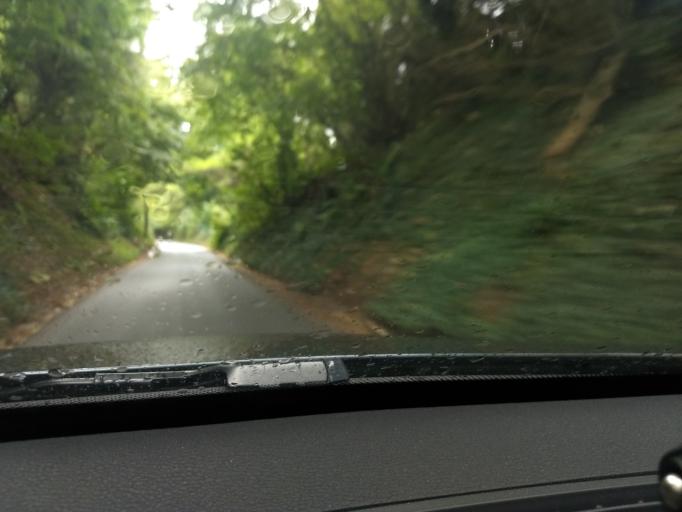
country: BE
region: Wallonia
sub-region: Province du Brabant Wallon
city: Braine-l'Alleud
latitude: 50.6727
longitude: 4.3732
